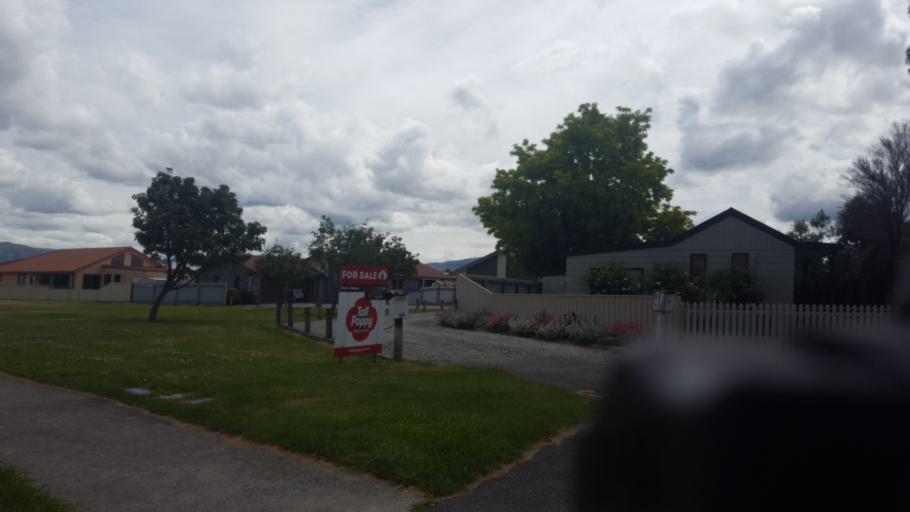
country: NZ
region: Otago
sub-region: Queenstown-Lakes District
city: Wanaka
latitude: -45.2532
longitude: 169.3852
